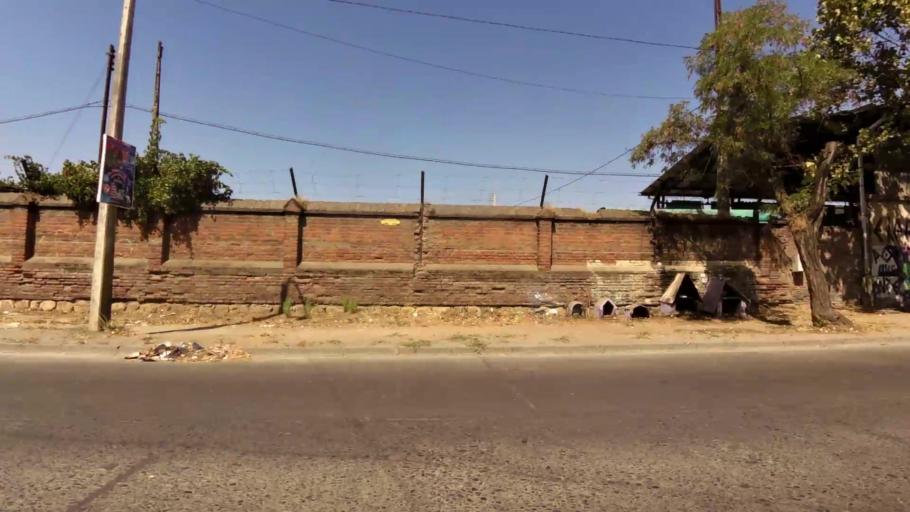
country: CL
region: Maule
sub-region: Provincia de Talca
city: Talca
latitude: -35.4320
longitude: -71.6506
